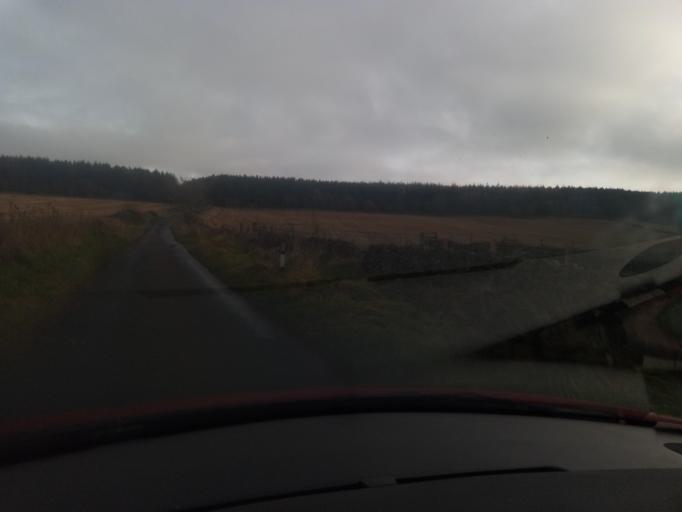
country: GB
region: Scotland
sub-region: The Scottish Borders
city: Jedburgh
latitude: 55.4868
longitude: -2.5946
